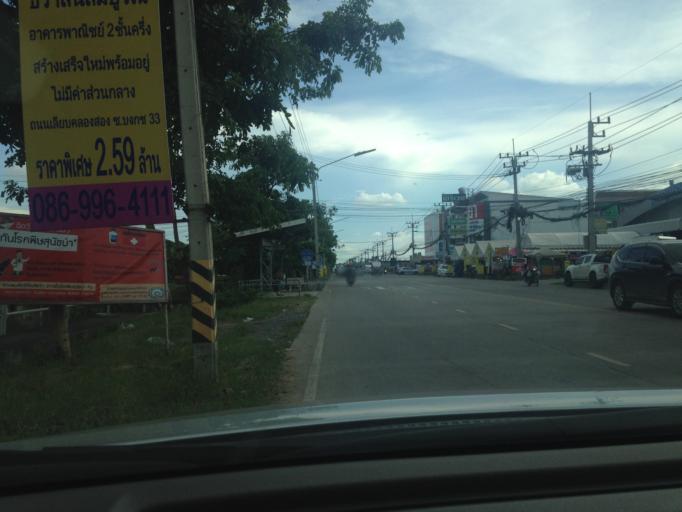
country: TH
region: Pathum Thani
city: Khlong Luang
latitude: 14.0488
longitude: 100.6636
